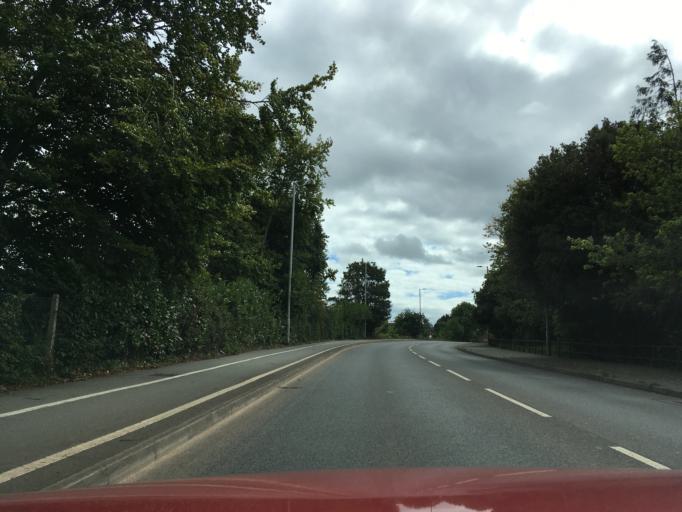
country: GB
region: England
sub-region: Devon
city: Heavitree
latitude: 50.7242
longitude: -3.4811
